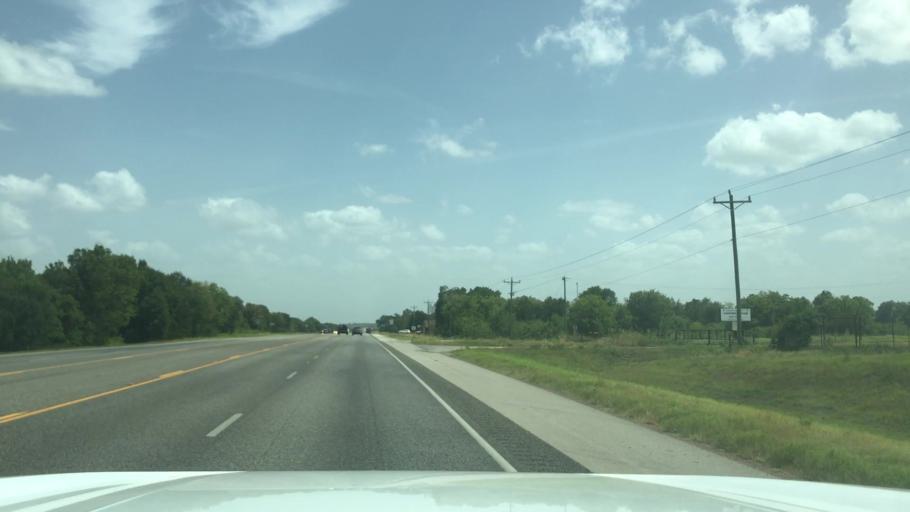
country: US
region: Texas
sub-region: Robertson County
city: Calvert
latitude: 30.9664
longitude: -96.6638
